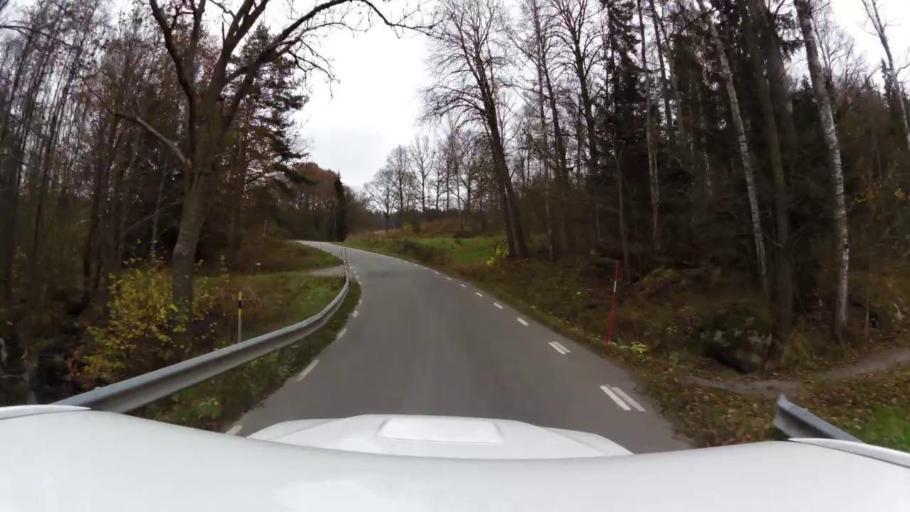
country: SE
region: OEstergoetland
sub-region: Kinda Kommun
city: Rimforsa
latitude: 58.1418
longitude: 15.6469
